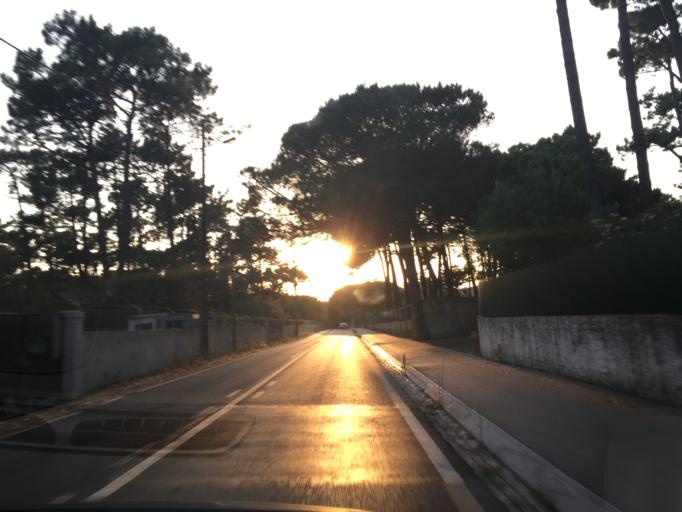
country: PT
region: Lisbon
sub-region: Sintra
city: Colares
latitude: 38.8312
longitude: -9.4477
